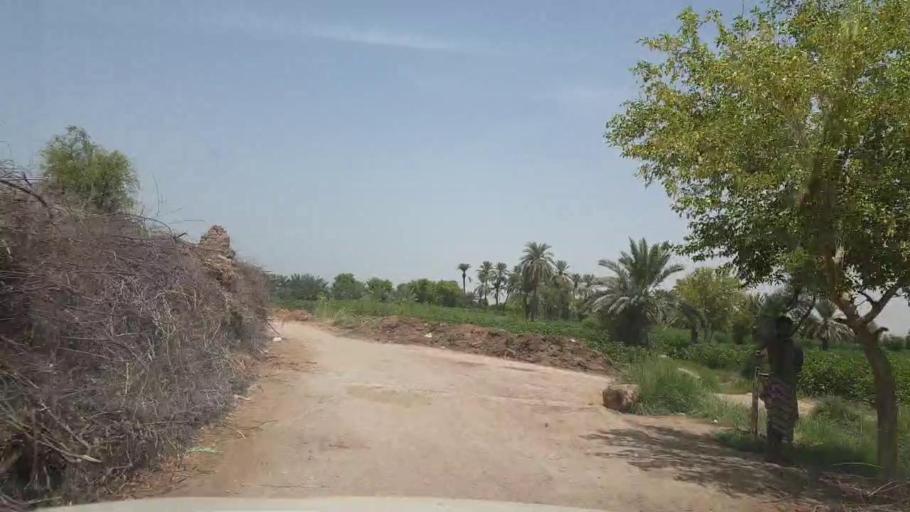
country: PK
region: Sindh
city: Bozdar
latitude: 27.1699
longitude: 68.6258
